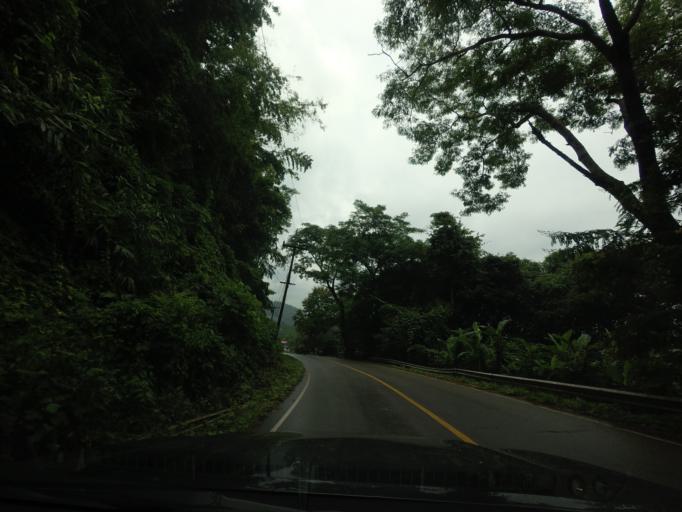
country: TH
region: Nong Khai
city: Sangkhom
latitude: 18.1420
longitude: 102.1906
